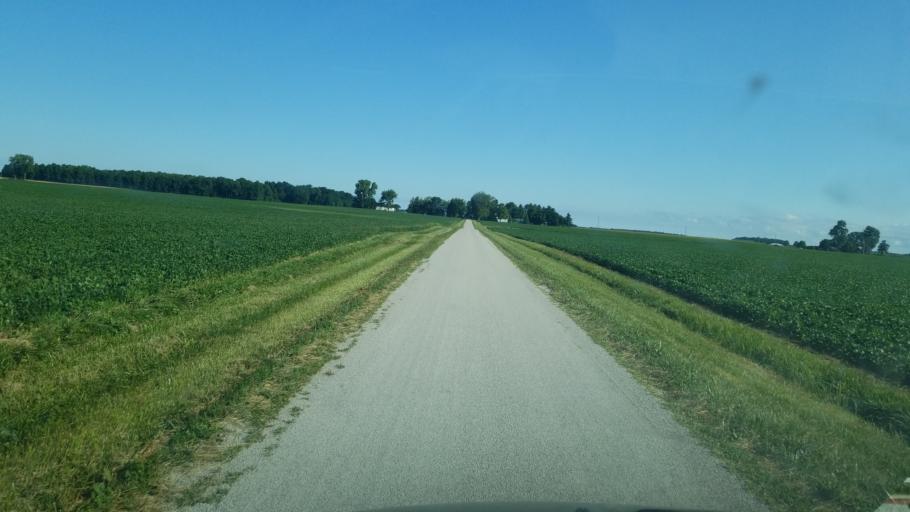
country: US
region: Ohio
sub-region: Wyandot County
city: Upper Sandusky
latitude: 40.9007
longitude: -83.2900
